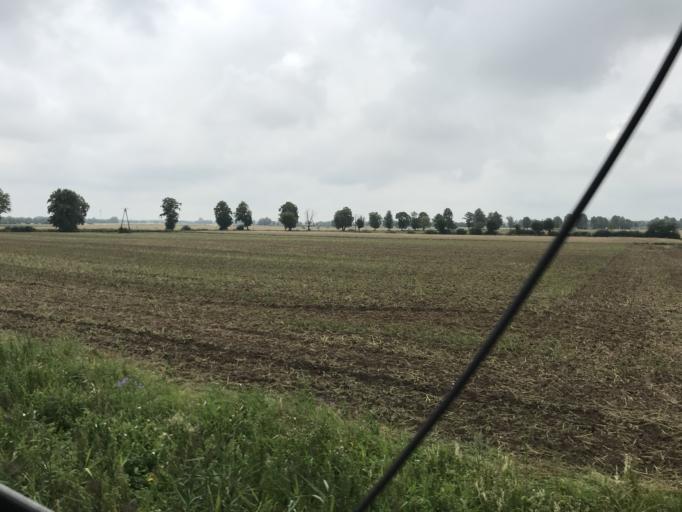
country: PL
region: Warmian-Masurian Voivodeship
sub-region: Powiat elblaski
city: Gronowo Elblaskie
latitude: 54.0930
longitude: 19.3138
